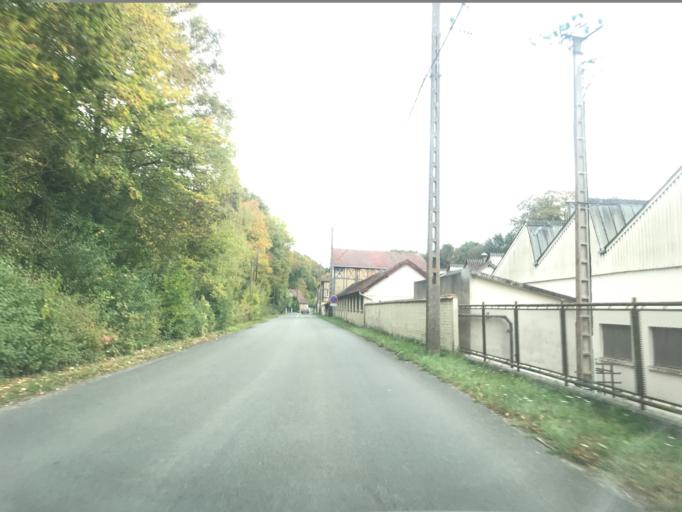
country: FR
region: Haute-Normandie
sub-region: Departement de l'Eure
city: Acquigny
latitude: 49.1663
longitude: 1.1915
